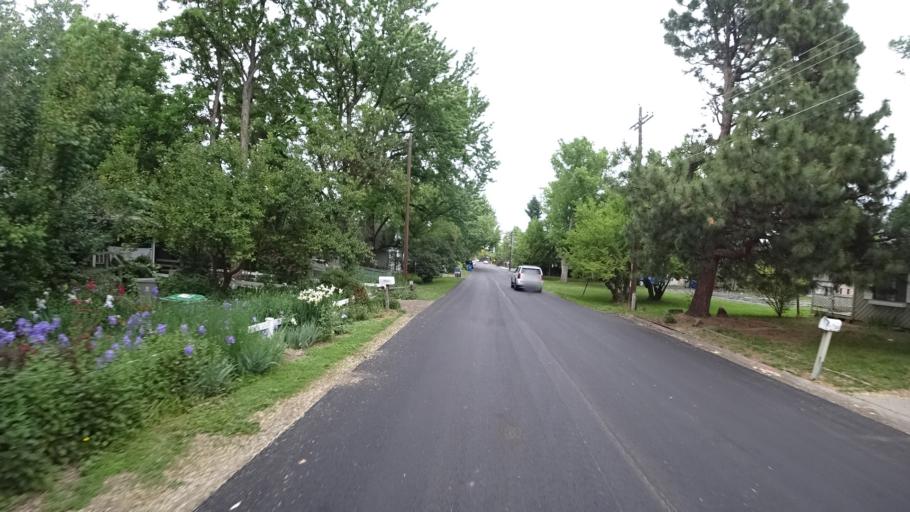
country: US
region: Idaho
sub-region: Ada County
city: Boise
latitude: 43.5798
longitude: -116.2038
